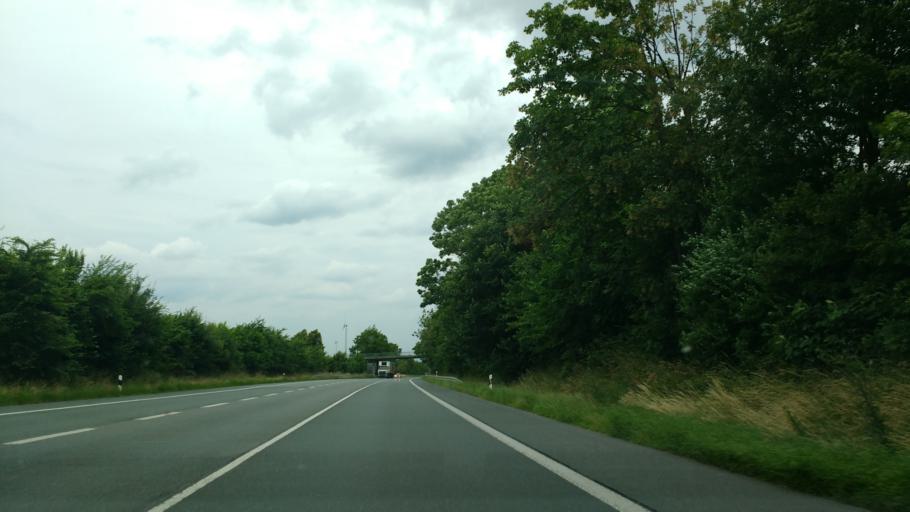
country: DE
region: North Rhine-Westphalia
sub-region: Regierungsbezirk Detmold
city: Wunnenberg
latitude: 51.5644
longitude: 8.7141
